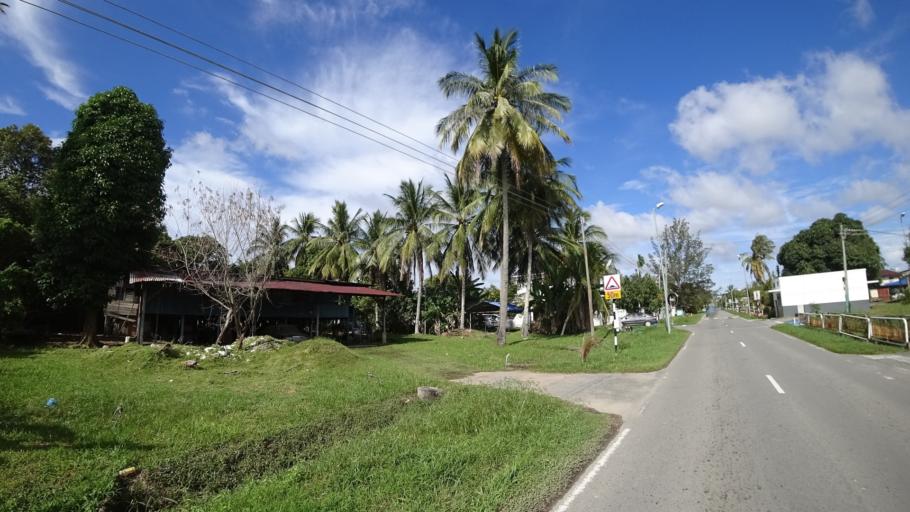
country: BN
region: Brunei and Muara
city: Bandar Seri Begawan
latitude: 4.9374
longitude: 114.9498
